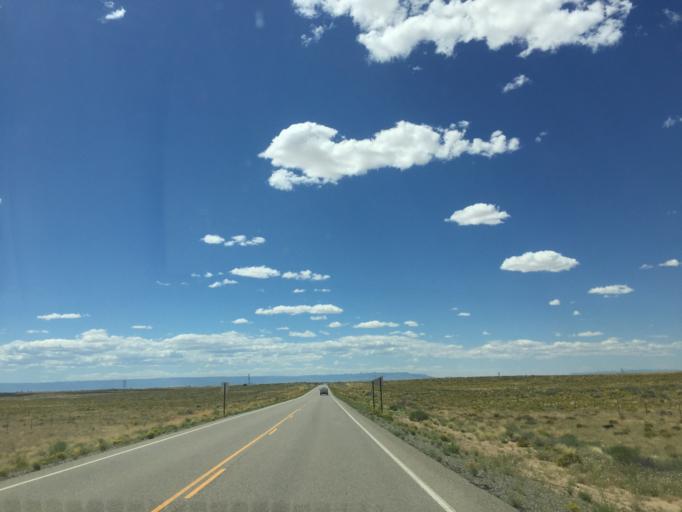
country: US
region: New Mexico
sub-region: San Juan County
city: Upper Fruitland
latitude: 36.4371
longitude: -108.2608
